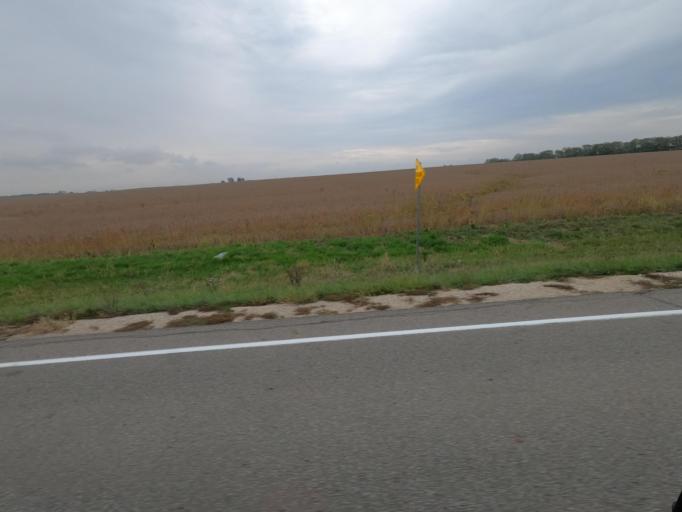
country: US
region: Iowa
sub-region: Van Buren County
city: Keosauqua
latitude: 40.8133
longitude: -91.7995
